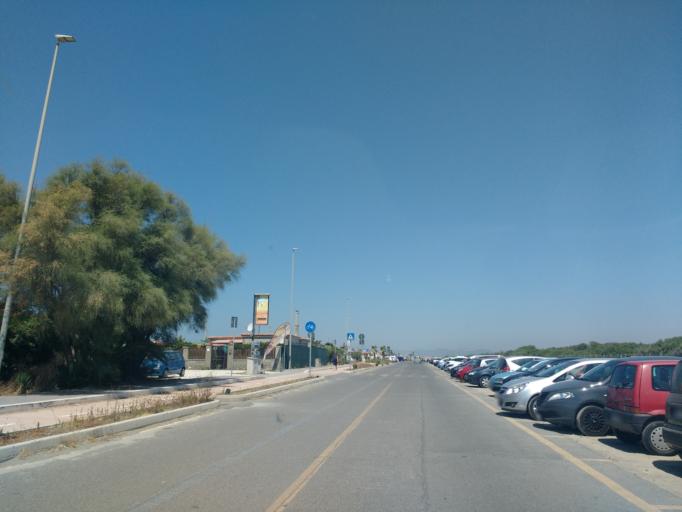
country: IT
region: Latium
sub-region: Citta metropolitana di Roma Capitale
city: Fregene
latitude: 41.8757
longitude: 12.1783
